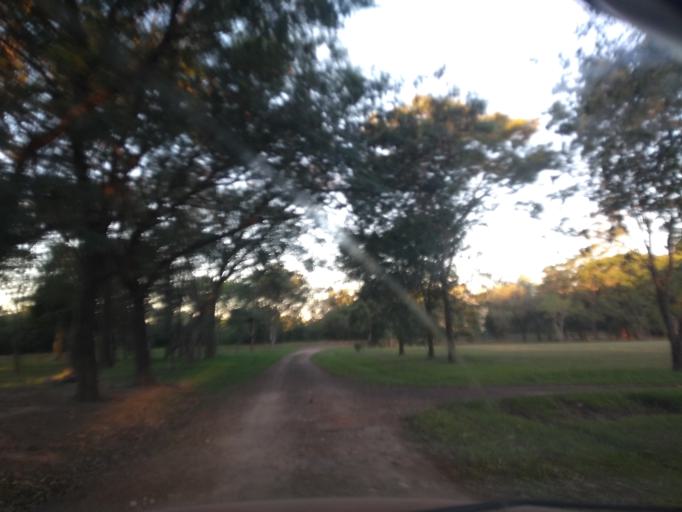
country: AR
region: Chaco
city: Fontana
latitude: -27.4232
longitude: -59.0053
